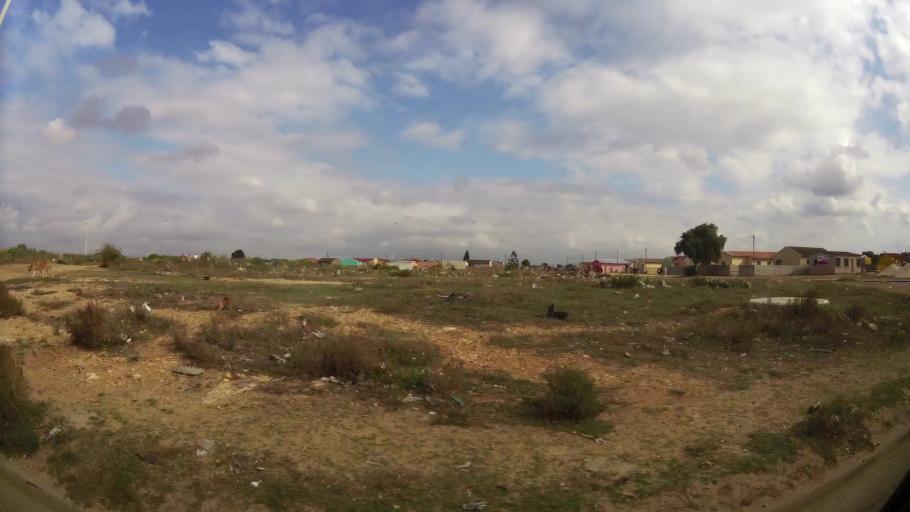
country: ZA
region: Eastern Cape
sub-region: Nelson Mandela Bay Metropolitan Municipality
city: Port Elizabeth
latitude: -33.8135
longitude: 25.5902
